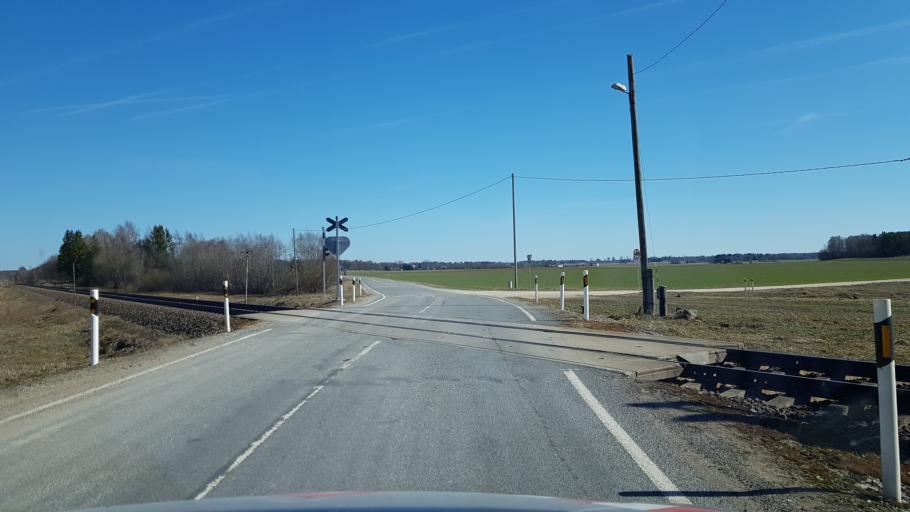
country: EE
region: Laeaene-Virumaa
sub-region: Someru vald
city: Someru
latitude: 59.3499
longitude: 26.4862
